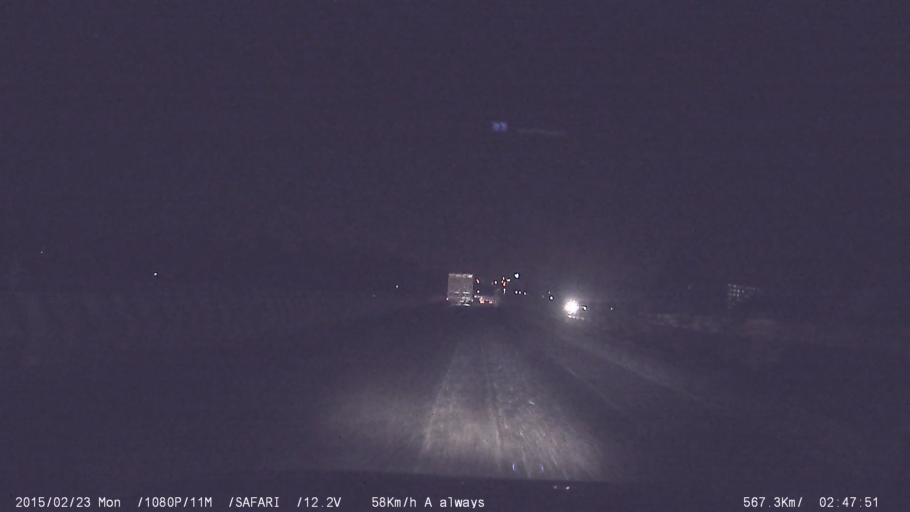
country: IN
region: Karnataka
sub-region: Bangalore Urban
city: Anekal
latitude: 12.8192
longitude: 77.6888
